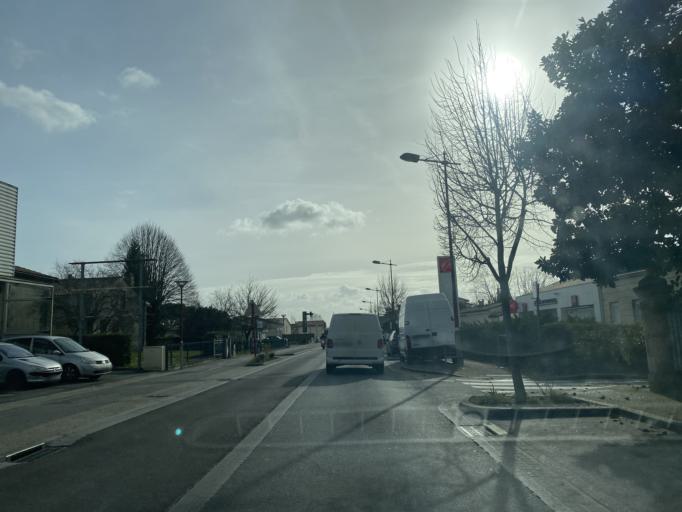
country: FR
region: Aquitaine
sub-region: Departement de la Gironde
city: Le Taillan-Medoc
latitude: 44.9084
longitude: -0.6690
